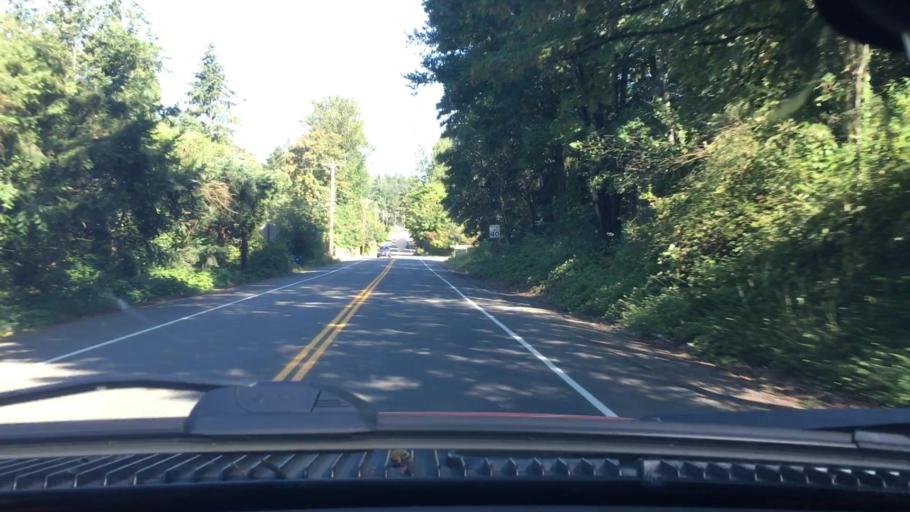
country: US
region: Washington
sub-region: King County
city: Covington
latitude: 47.3424
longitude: -122.1325
